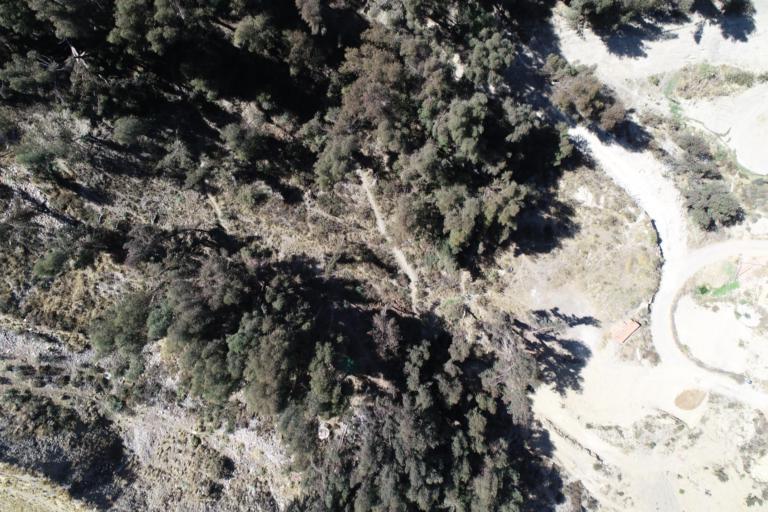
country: BO
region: La Paz
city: La Paz
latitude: -16.5412
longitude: -68.1564
